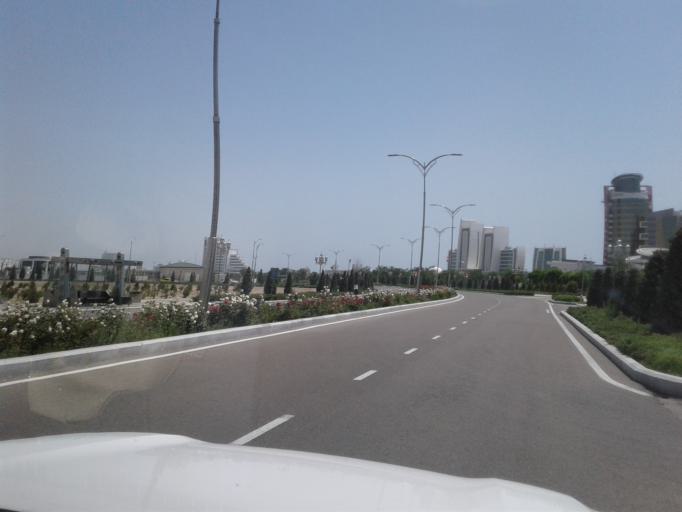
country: TM
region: Balkan
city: Turkmenbasy
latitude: 39.9647
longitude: 52.8332
